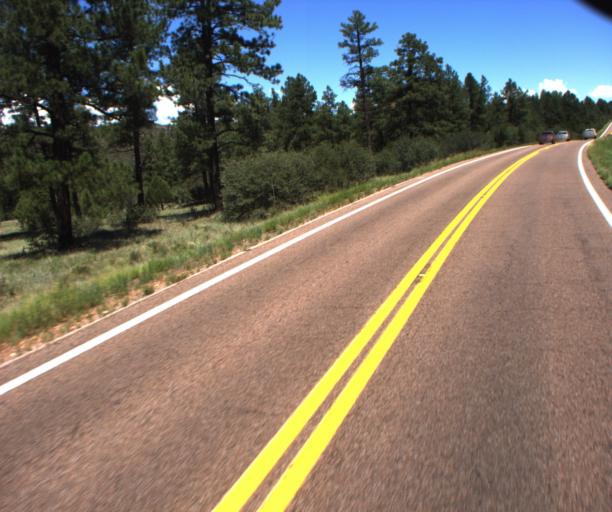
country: US
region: Arizona
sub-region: Navajo County
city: Linden
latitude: 34.0768
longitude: -110.1923
